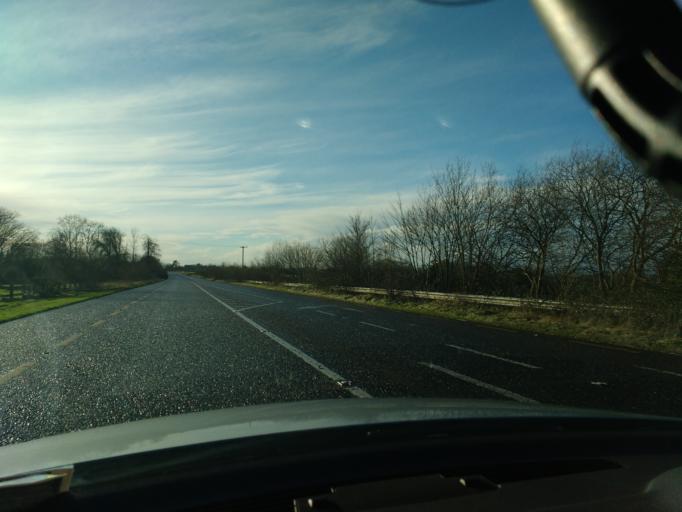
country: IE
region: Munster
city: Thurles
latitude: 52.6560
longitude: -7.7080
